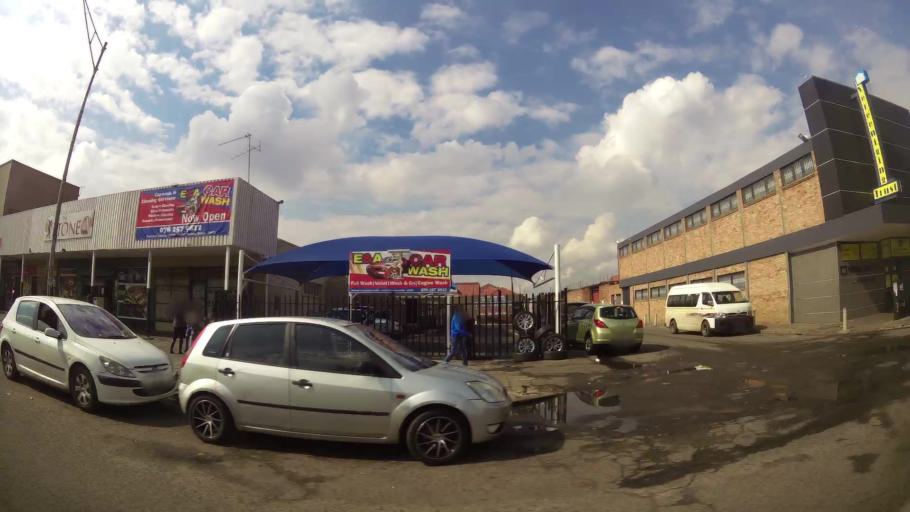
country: ZA
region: Gauteng
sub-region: Sedibeng District Municipality
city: Vereeniging
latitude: -26.6766
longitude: 27.9290
